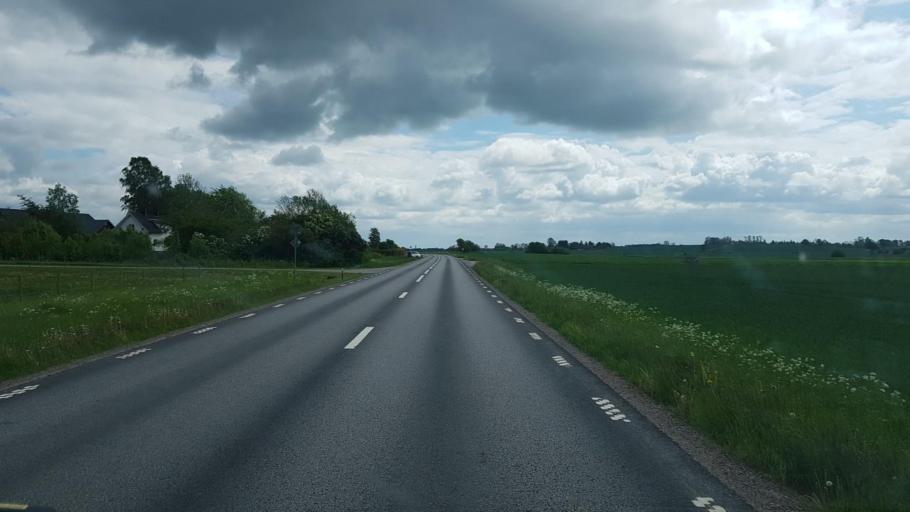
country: SE
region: OEstergoetland
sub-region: Motala Kommun
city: Borensberg
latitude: 58.4838
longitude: 15.2145
